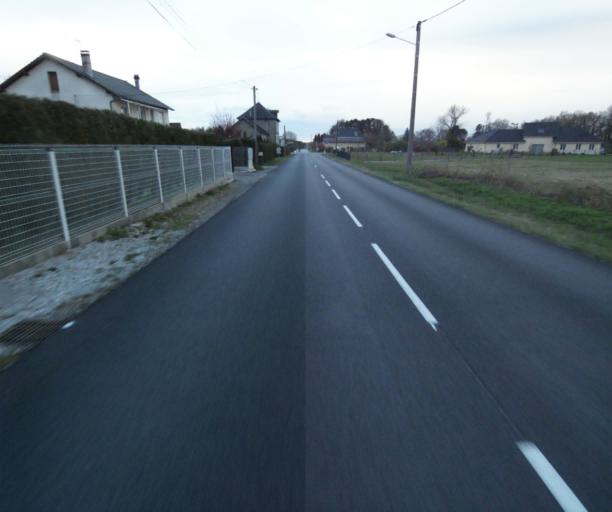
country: FR
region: Limousin
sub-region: Departement de la Correze
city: Correze
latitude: 45.3391
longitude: 1.8754
